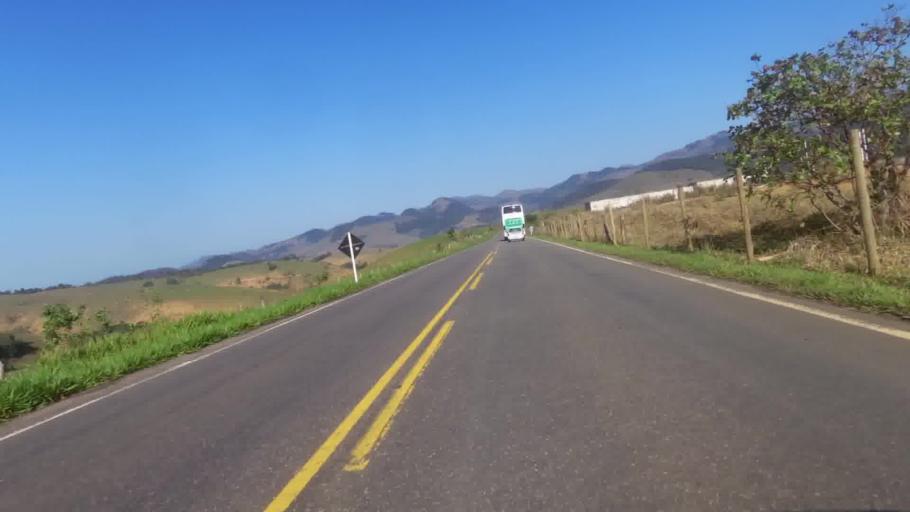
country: BR
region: Espirito Santo
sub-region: Alfredo Chaves
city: Alfredo Chaves
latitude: -20.6702
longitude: -40.7287
